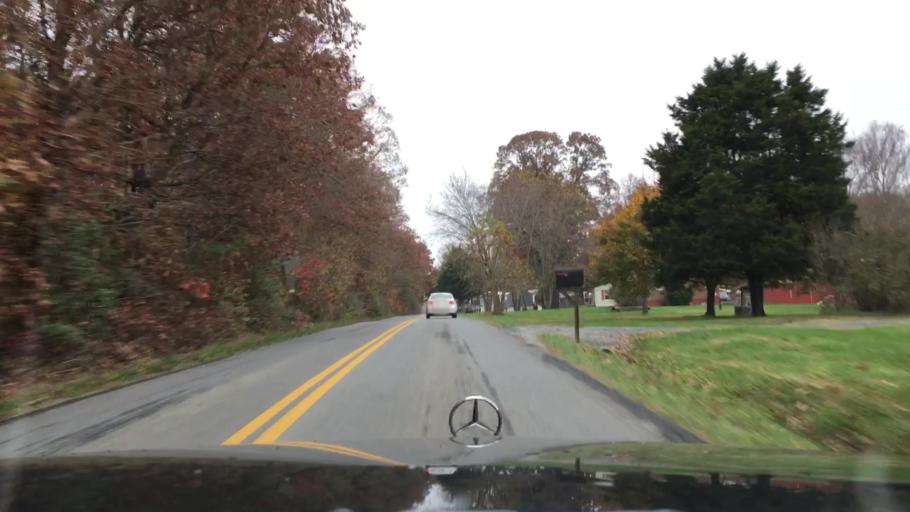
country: US
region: Virginia
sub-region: Campbell County
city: Timberlake
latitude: 37.2932
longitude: -79.2793
